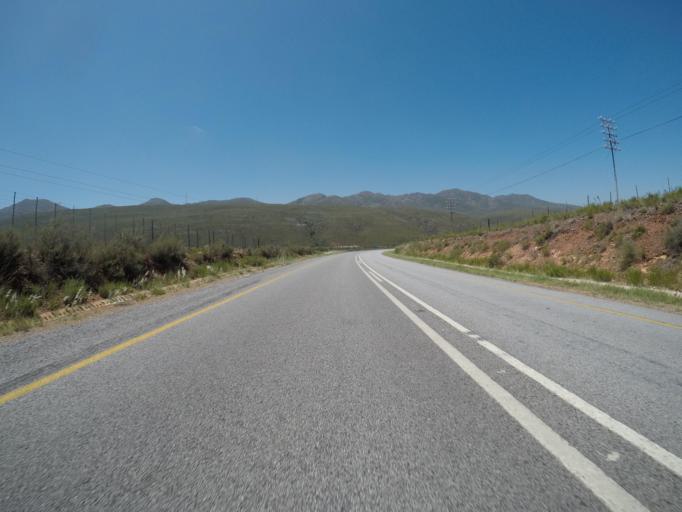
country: ZA
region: Eastern Cape
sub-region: Cacadu District Municipality
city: Kareedouw
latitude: -33.9437
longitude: 24.3060
